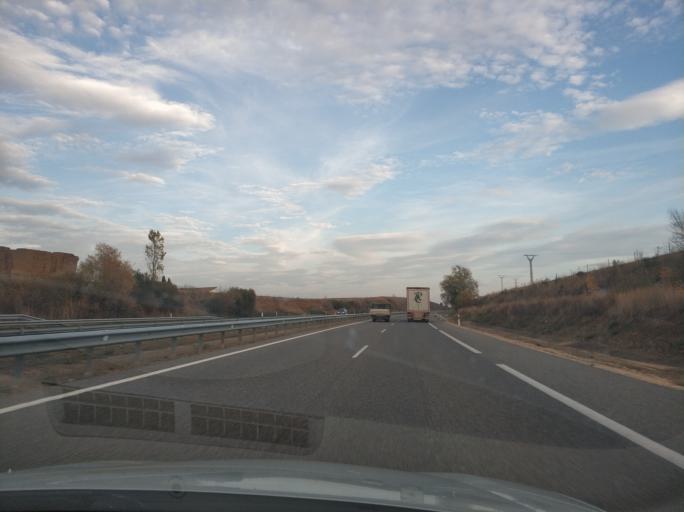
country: ES
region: Castille and Leon
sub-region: Provincia de Burgos
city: Melgar de Fernamental
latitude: 42.4116
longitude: -4.2437
